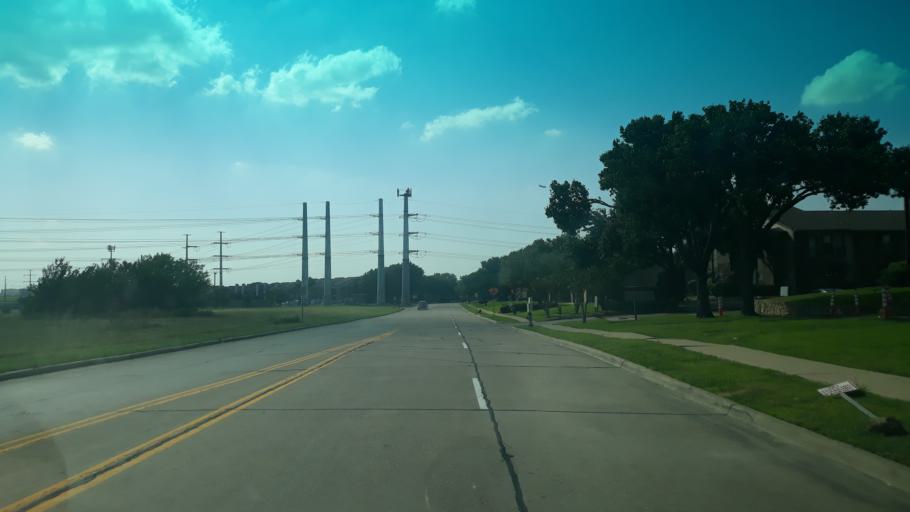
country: US
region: Texas
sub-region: Tarrant County
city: Euless
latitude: 32.8603
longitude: -97.0111
